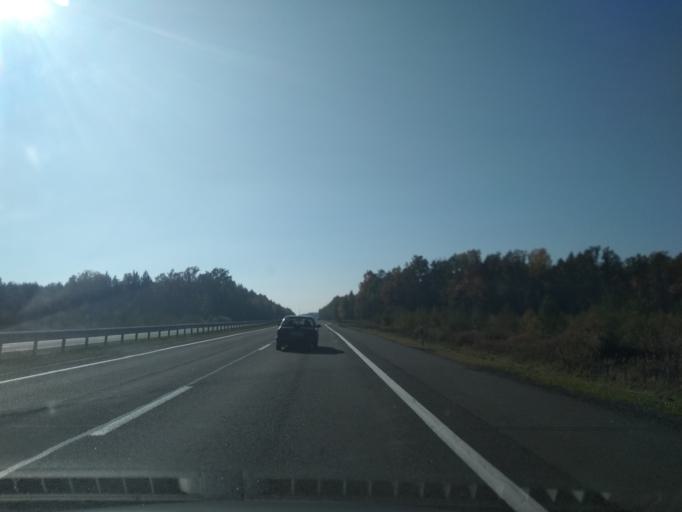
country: BY
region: Brest
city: Ivatsevichy
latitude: 52.8224
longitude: 25.5889
